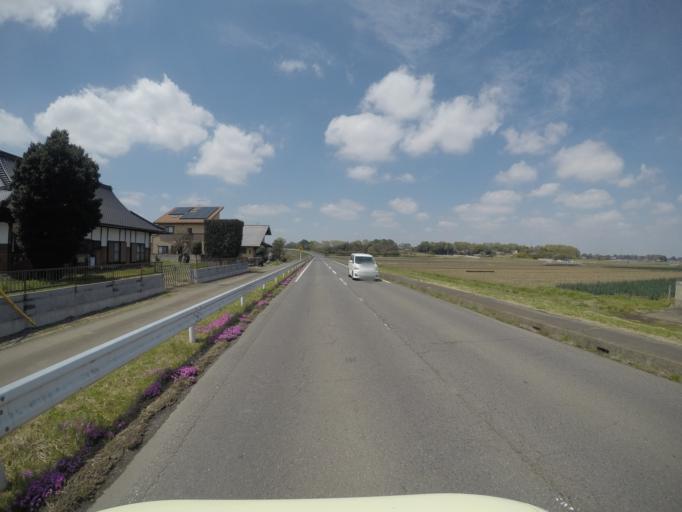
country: JP
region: Ibaraki
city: Shimodate
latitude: 36.3375
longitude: 139.9822
